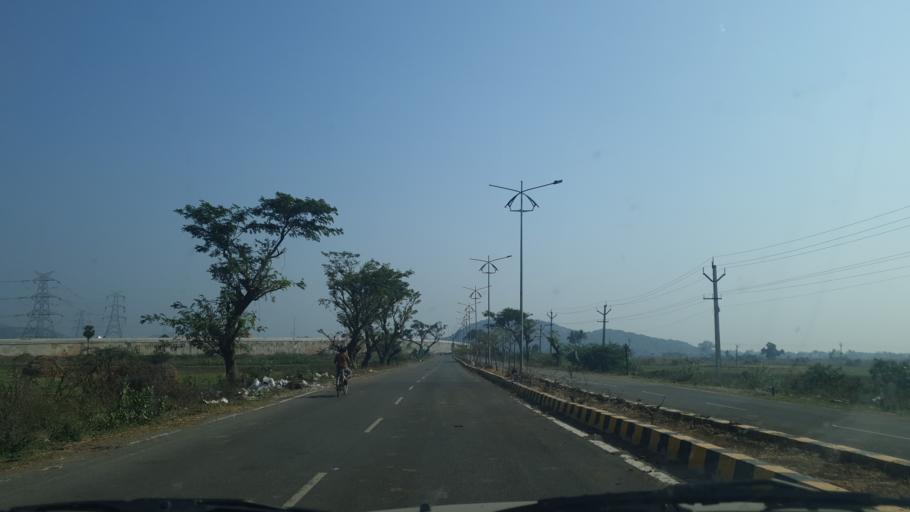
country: IN
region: Andhra Pradesh
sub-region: Srikakulam
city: Tekkali
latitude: 18.6163
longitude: 84.2400
